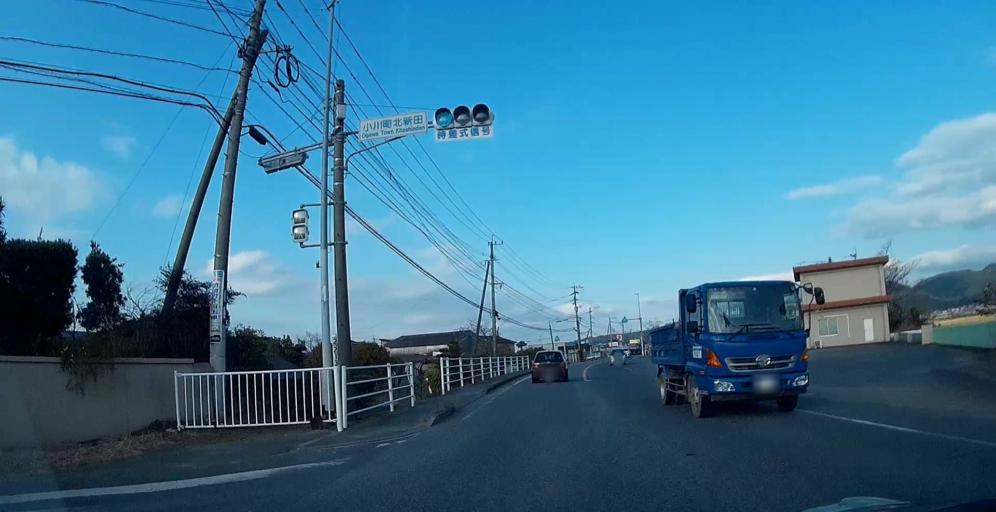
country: JP
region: Kumamoto
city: Matsubase
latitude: 32.6040
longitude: 130.7022
